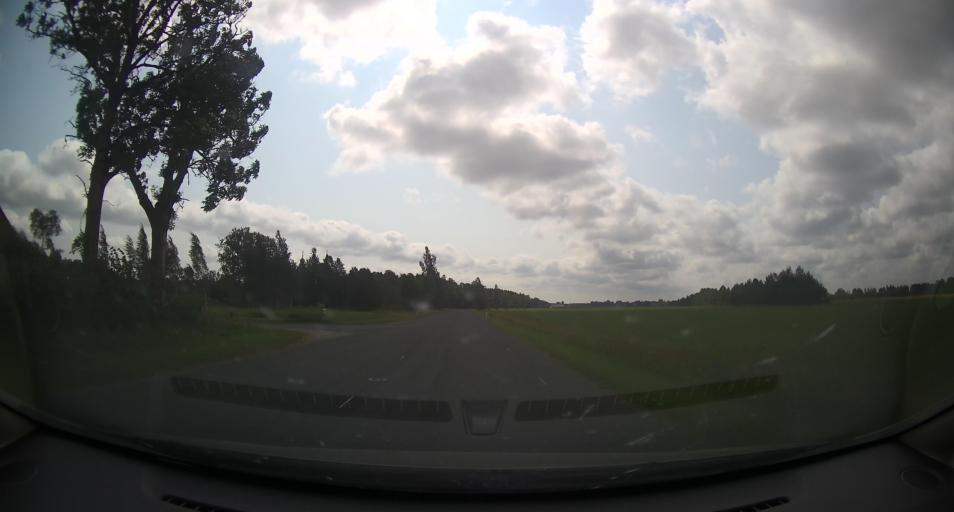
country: EE
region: Paernumaa
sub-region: Audru vald
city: Audru
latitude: 58.4881
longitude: 24.3355
